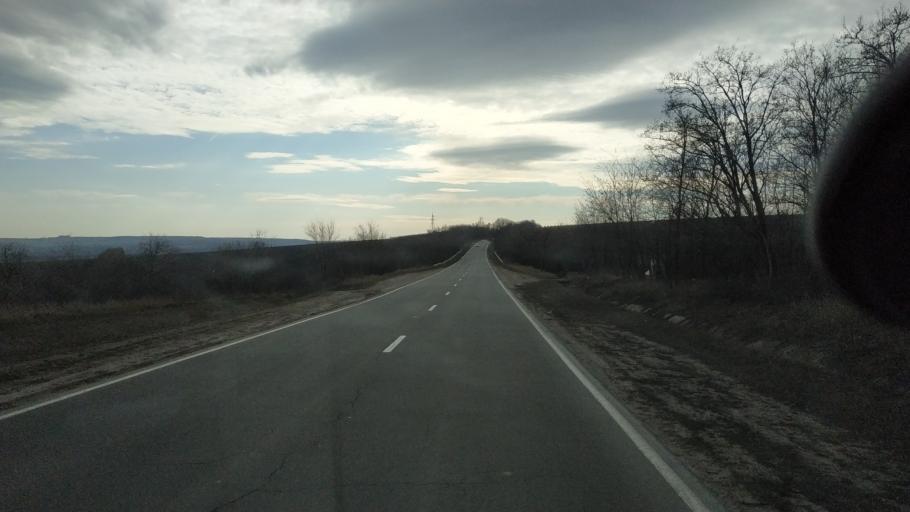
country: MD
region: Chisinau
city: Vadul lui Voda
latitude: 47.0830
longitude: 29.0370
